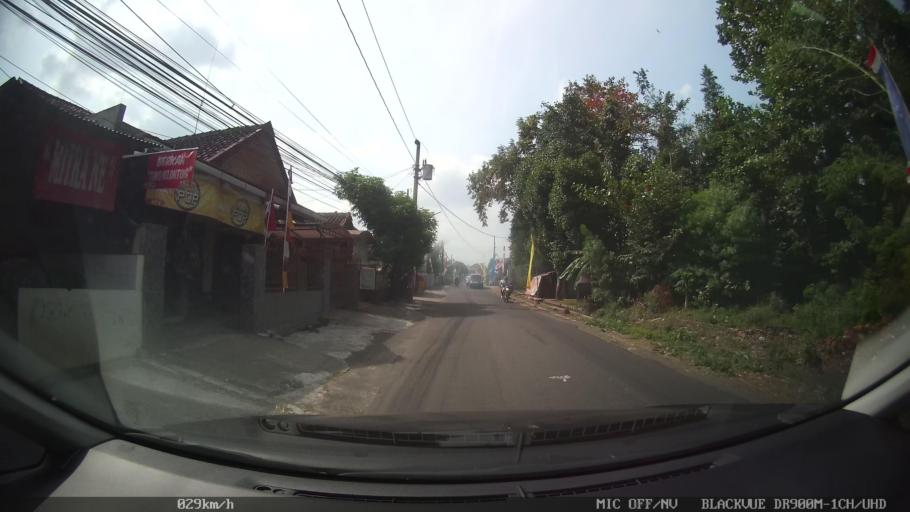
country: ID
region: Daerah Istimewa Yogyakarta
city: Depok
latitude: -7.7941
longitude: 110.4457
